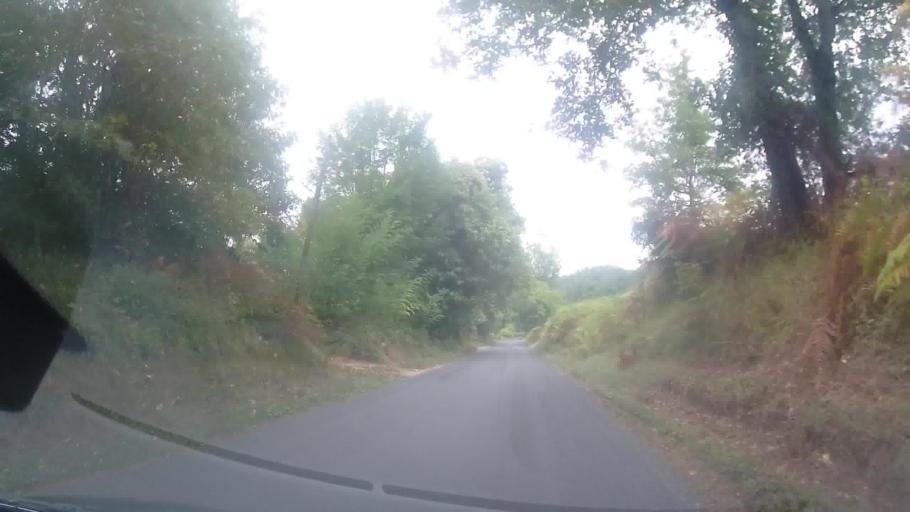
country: FR
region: Aquitaine
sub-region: Departement de la Dordogne
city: Eyvigues-et-Eybenes
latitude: 44.8443
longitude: 1.3648
